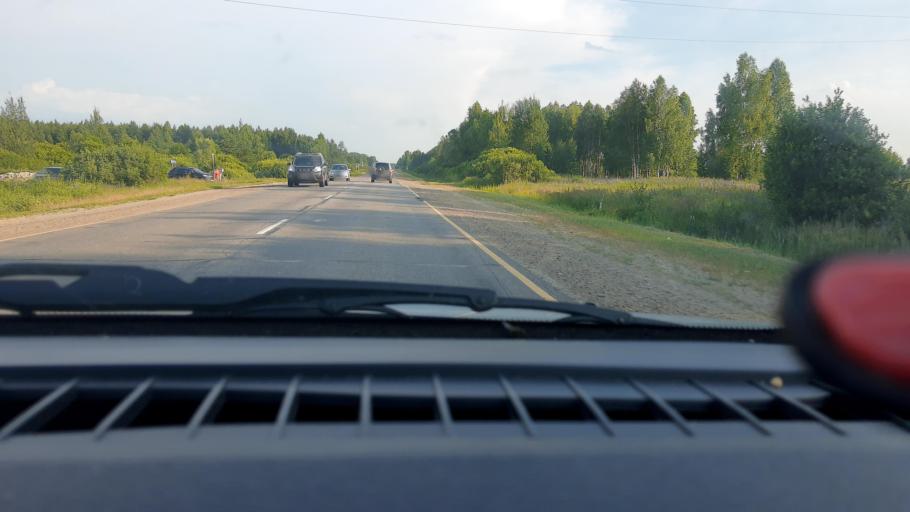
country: RU
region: Nizjnij Novgorod
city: Arzamas
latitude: 55.4000
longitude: 43.9161
